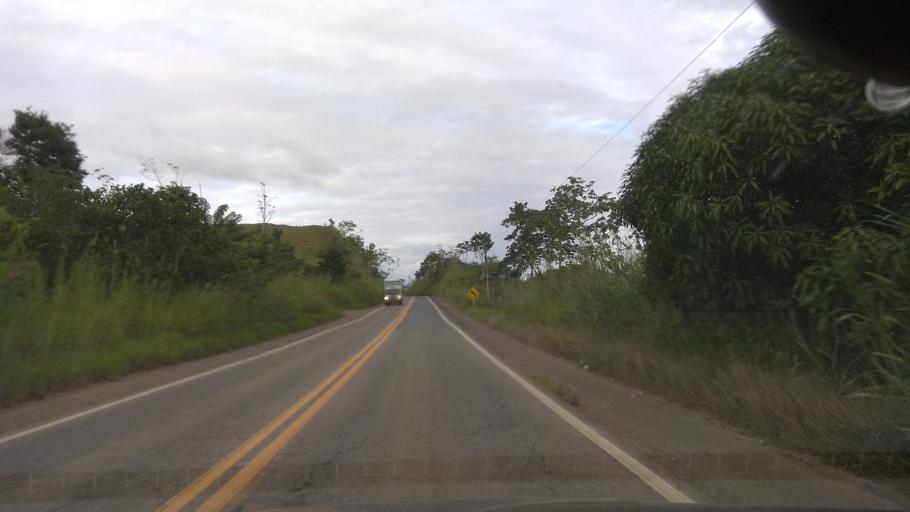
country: BR
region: Bahia
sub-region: Ipiau
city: Ipiau
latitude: -14.1522
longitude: -39.6988
